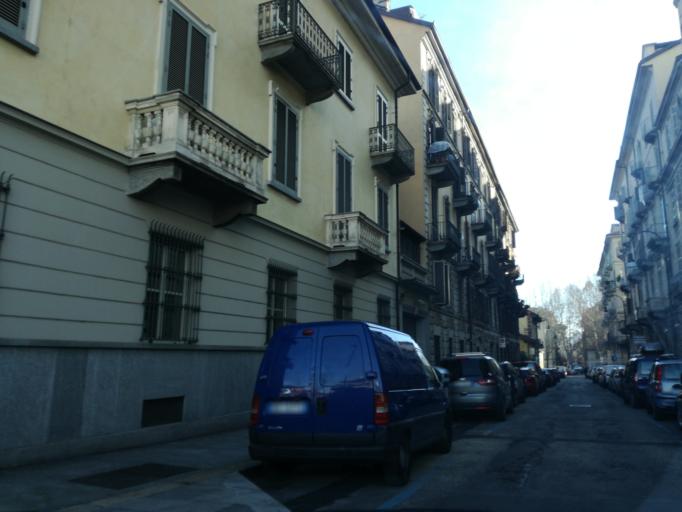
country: IT
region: Piedmont
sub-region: Provincia di Torino
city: Turin
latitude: 45.0789
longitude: 7.6703
